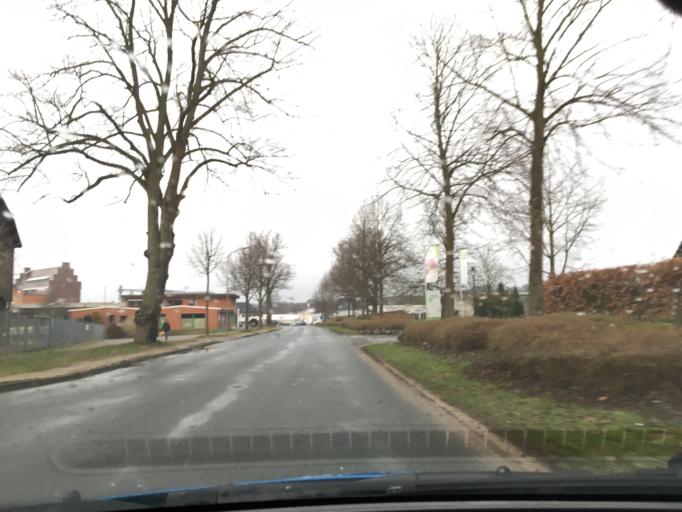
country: DE
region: Schleswig-Holstein
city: Molln
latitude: 53.6223
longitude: 10.6768
